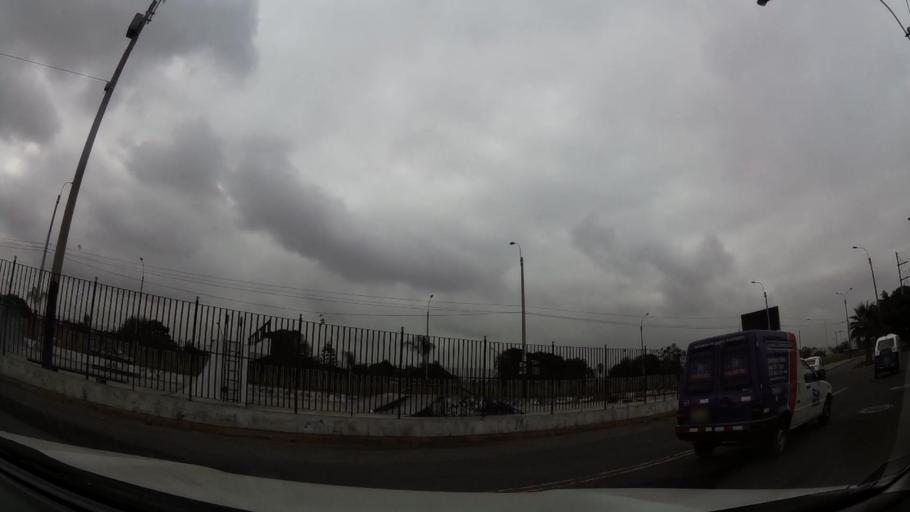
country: PE
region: Lima
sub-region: Lima
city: Surco
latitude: -12.1706
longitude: -77.0177
